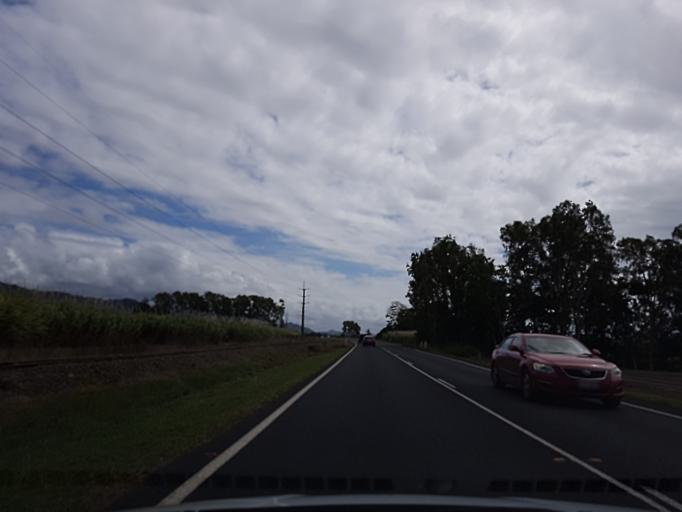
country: AU
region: Queensland
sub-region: Cairns
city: Port Douglas
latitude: -16.5094
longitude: 145.4421
